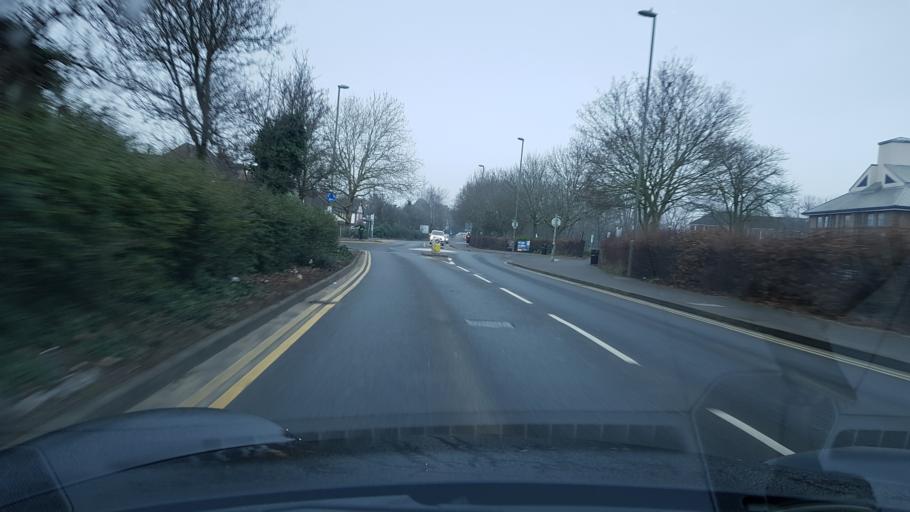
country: GB
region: England
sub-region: Surrey
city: Guildford
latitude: 51.2441
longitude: -0.5716
